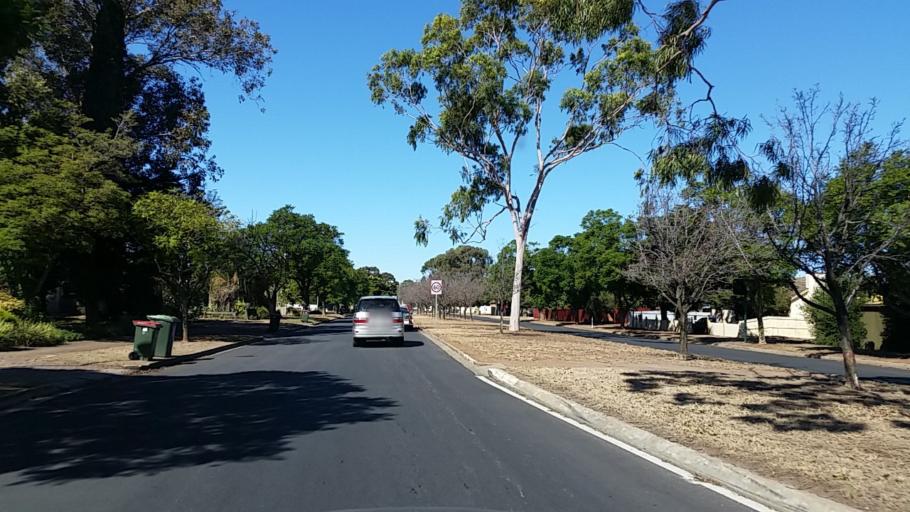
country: AU
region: South Australia
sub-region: Salisbury
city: Elizabeth
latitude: -34.7055
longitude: 138.6747
